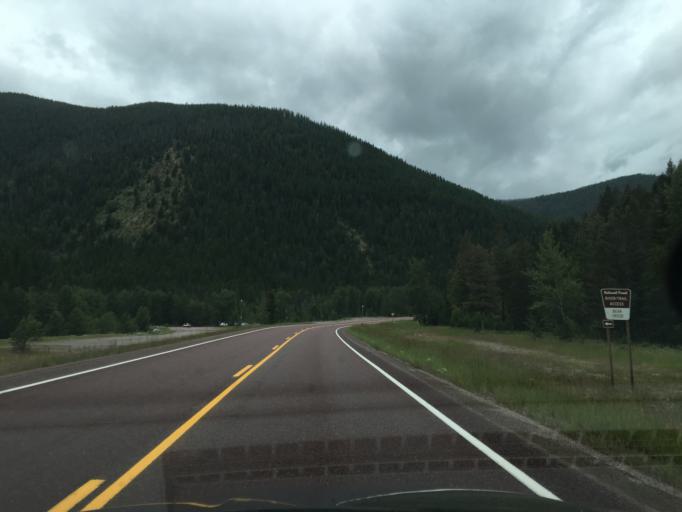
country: US
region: Montana
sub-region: Flathead County
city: Bigfork
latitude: 48.2340
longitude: -113.5629
